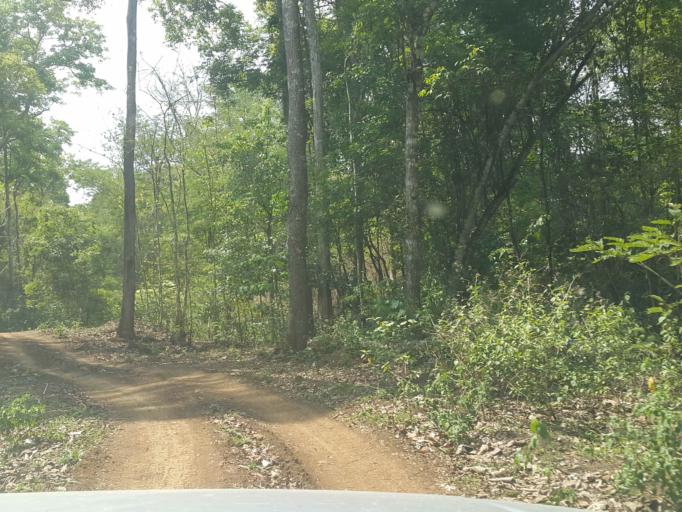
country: TH
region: Chiang Mai
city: Wiang Haeng
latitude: 19.3359
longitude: 98.7173
